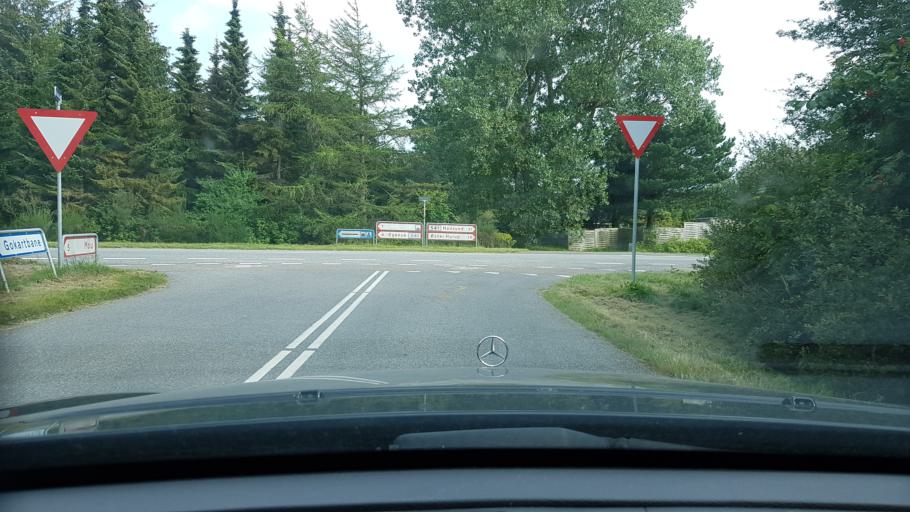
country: DK
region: North Denmark
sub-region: Alborg Kommune
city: Hals
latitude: 56.9233
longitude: 10.2611
